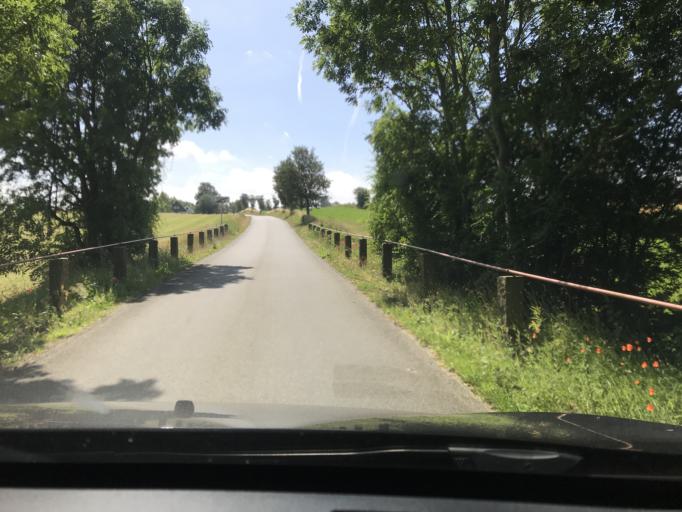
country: DK
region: South Denmark
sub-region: AEro Kommune
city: AEroskobing
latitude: 54.9099
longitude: 10.3022
